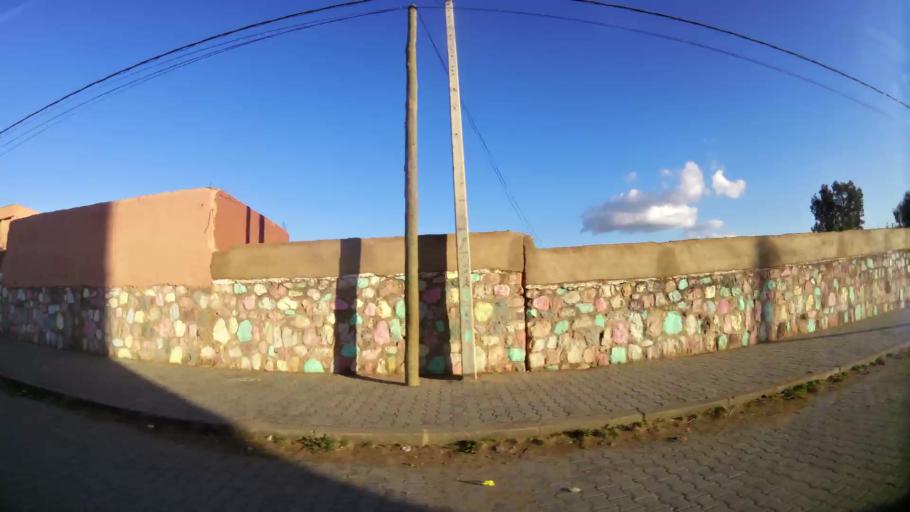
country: MA
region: Marrakech-Tensift-Al Haouz
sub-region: Kelaa-Des-Sraghna
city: Sidi Abdallah
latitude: 32.2469
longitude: -7.9481
